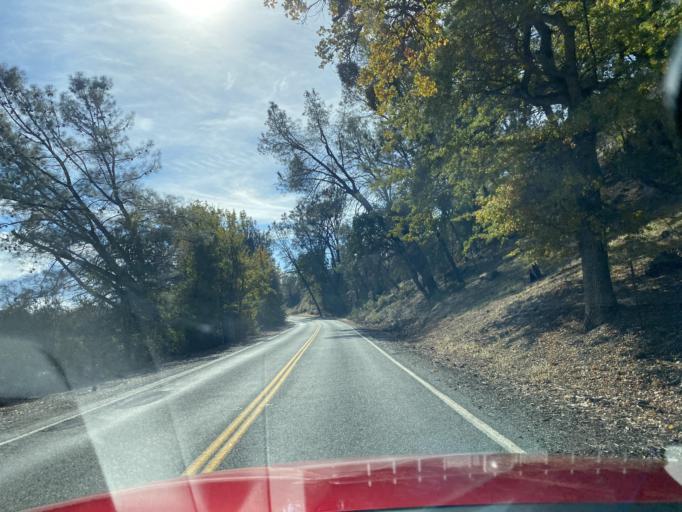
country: US
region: California
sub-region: Glenn County
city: Willows
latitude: 39.4459
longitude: -122.5136
